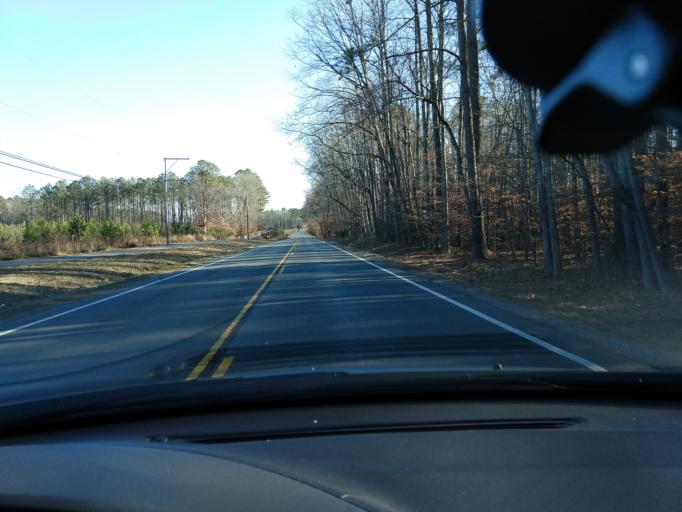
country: US
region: Virginia
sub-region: Charles City County
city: Charles City
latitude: 37.3205
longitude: -76.9734
